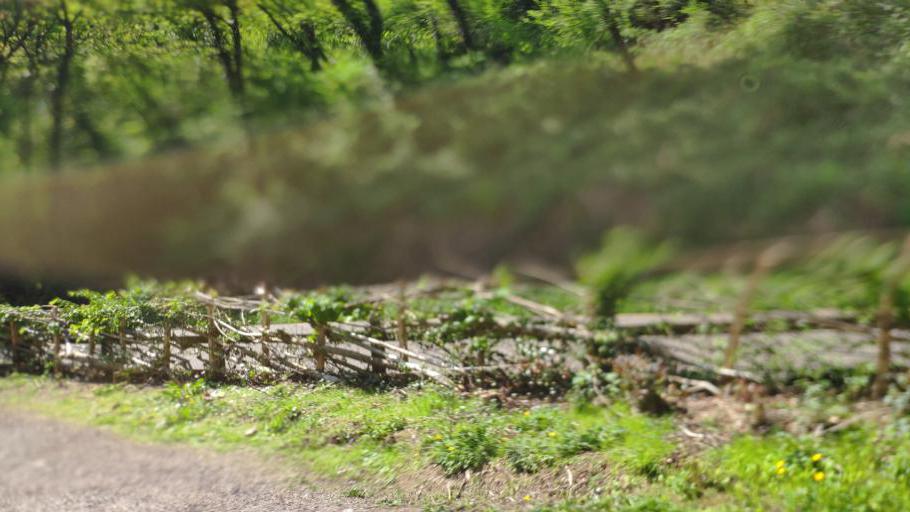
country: IE
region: Munster
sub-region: County Cork
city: Blarney
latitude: 51.9461
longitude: -8.5674
